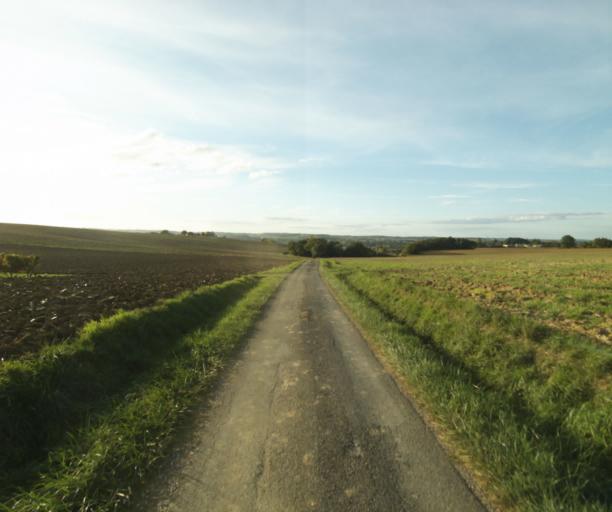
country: FR
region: Midi-Pyrenees
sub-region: Departement du Gers
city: Gondrin
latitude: 43.8754
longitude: 0.3076
